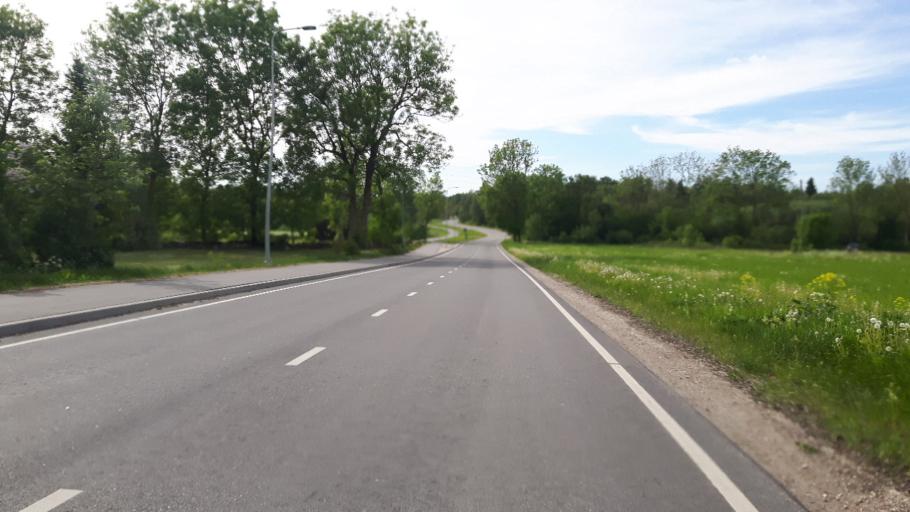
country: EE
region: Harju
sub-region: Joelaehtme vald
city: Loo
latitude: 59.4270
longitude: 24.9905
